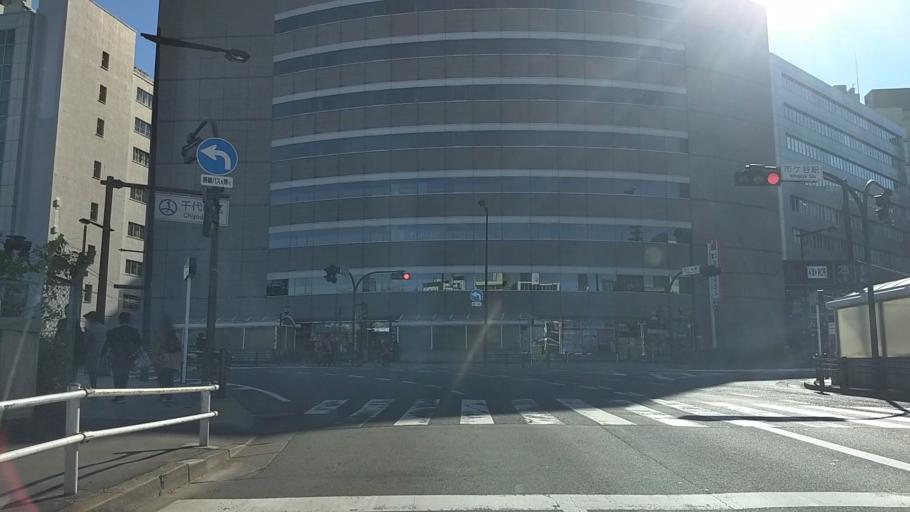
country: JP
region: Tokyo
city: Tokyo
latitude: 35.6914
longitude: 139.7358
